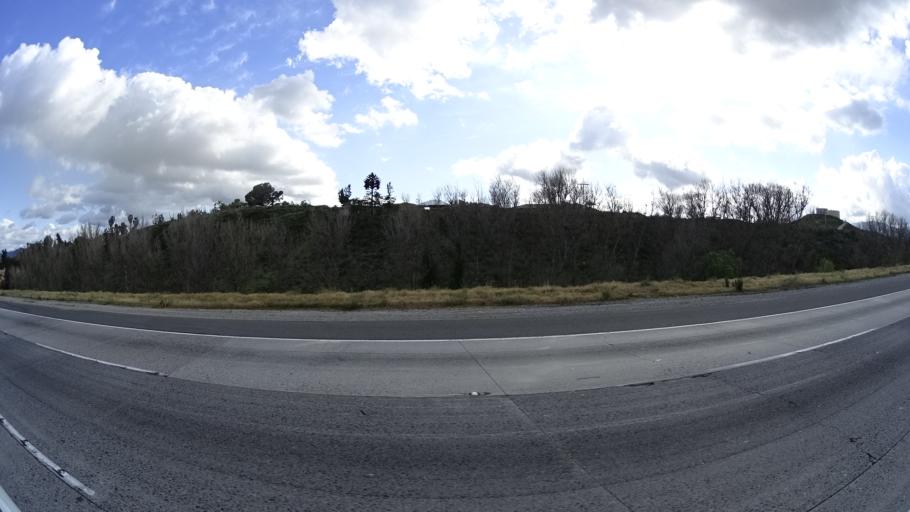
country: US
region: California
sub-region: Riverside County
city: Murrieta
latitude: 33.5831
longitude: -117.2304
